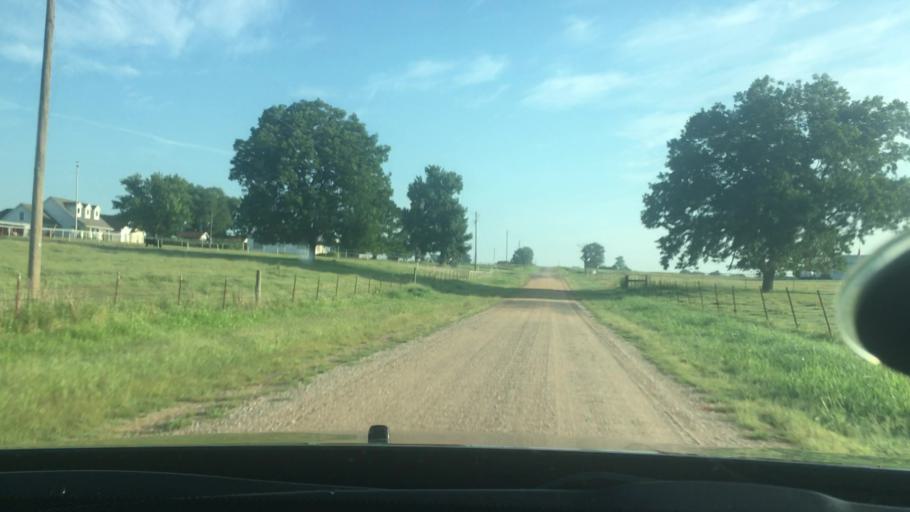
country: US
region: Oklahoma
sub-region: Pontotoc County
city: Ada
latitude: 34.8166
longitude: -96.7748
